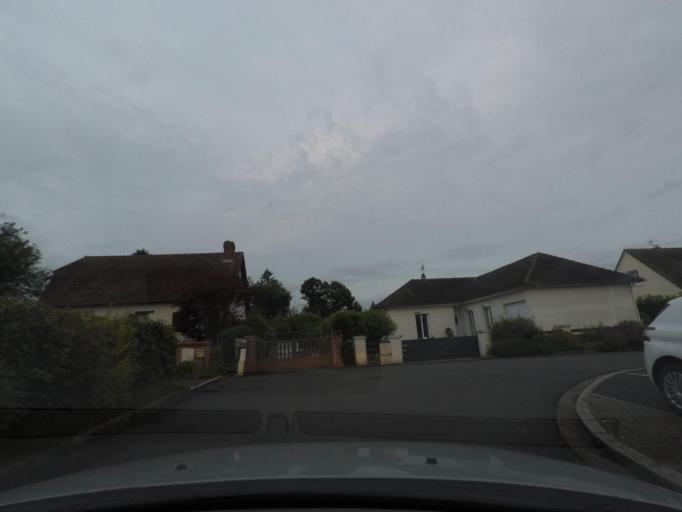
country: FR
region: Haute-Normandie
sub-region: Departement de la Seine-Maritime
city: Houppeville
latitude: 49.5438
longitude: 1.1160
